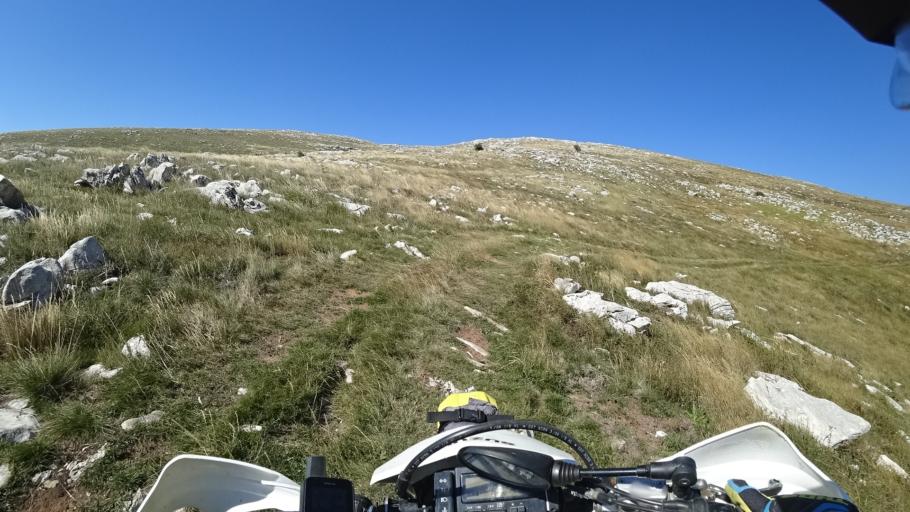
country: HR
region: Splitsko-Dalmatinska
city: Hrvace
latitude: 43.9196
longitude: 16.6056
